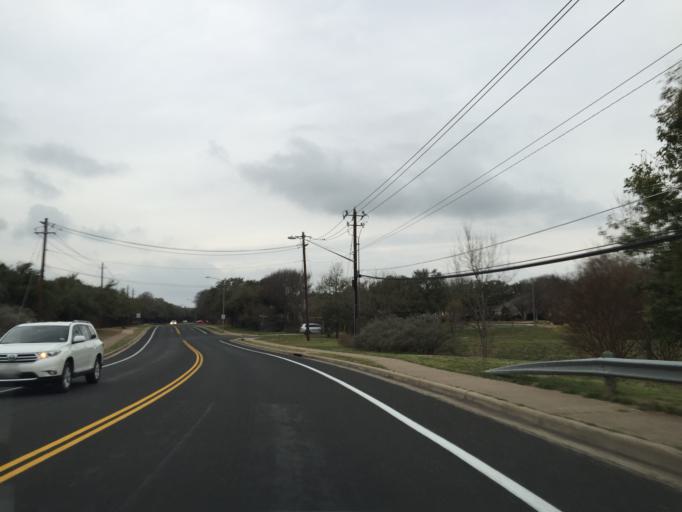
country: US
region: Texas
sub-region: Travis County
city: Lost Creek
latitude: 30.2447
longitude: -97.8365
